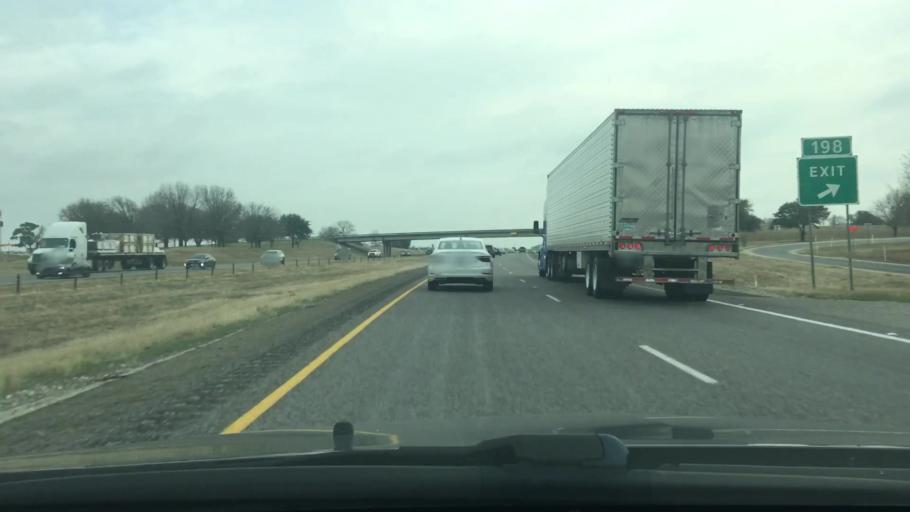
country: US
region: Texas
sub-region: Freestone County
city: Fairfield
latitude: 31.7294
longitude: -96.1813
